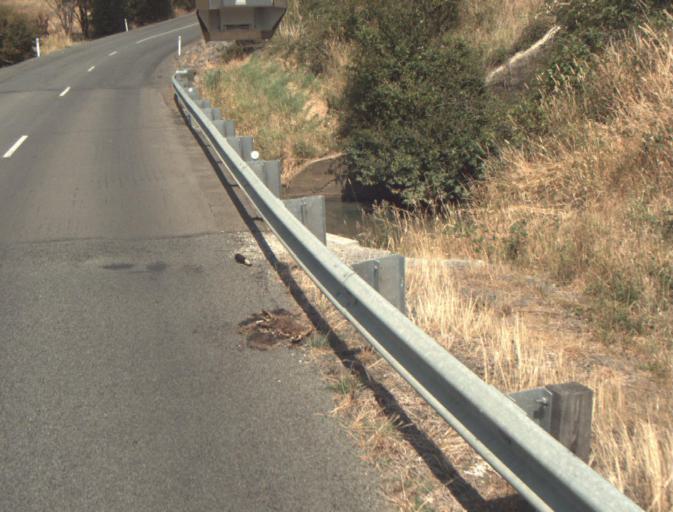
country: AU
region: Tasmania
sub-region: Launceston
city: Newstead
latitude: -41.4689
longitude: 147.1875
